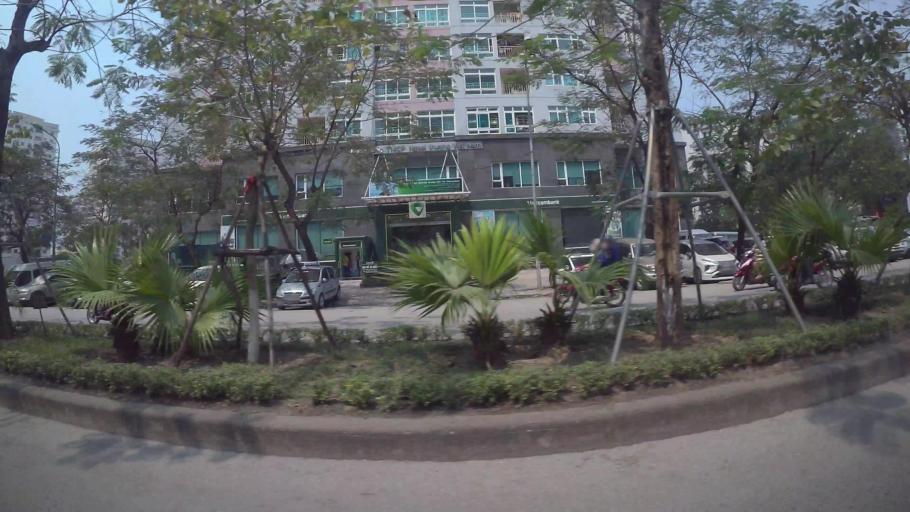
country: VN
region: Ha Noi
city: Thanh Xuan
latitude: 21.0043
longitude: 105.8061
